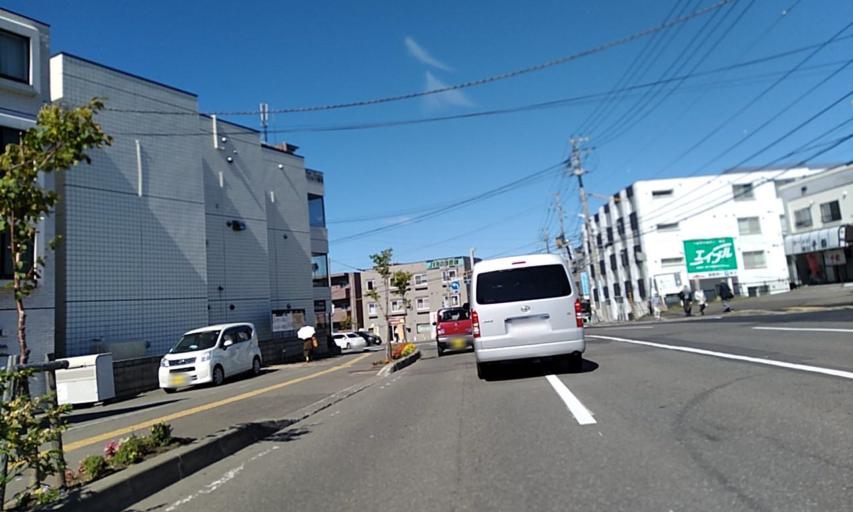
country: JP
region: Hokkaido
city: Sapporo
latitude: 43.0148
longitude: 141.3687
